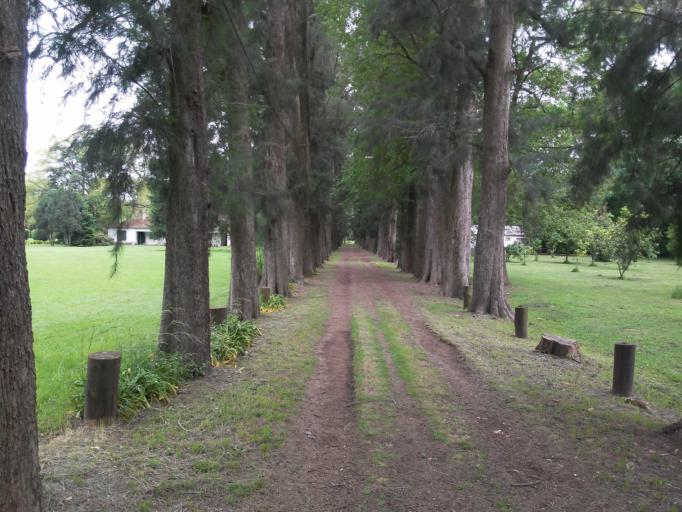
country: AR
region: Buenos Aires
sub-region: Partido de General Rodriguez
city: General Rodriguez
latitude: -34.5975
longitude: -58.9932
